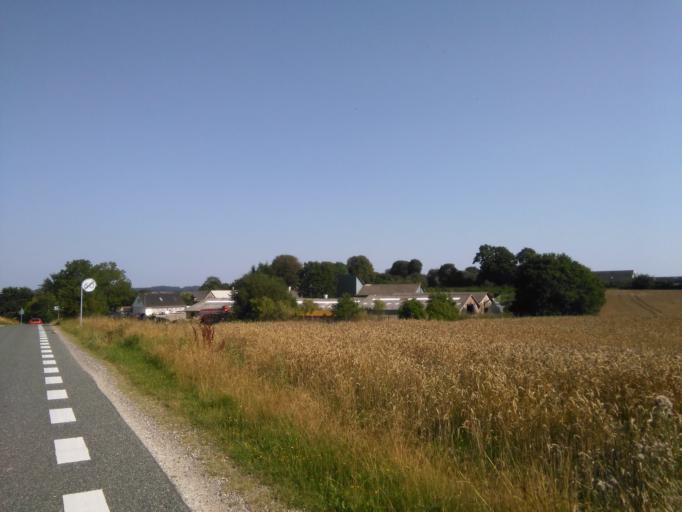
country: DK
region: Central Jutland
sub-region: Arhus Kommune
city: Framlev
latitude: 56.1344
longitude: 10.0060
